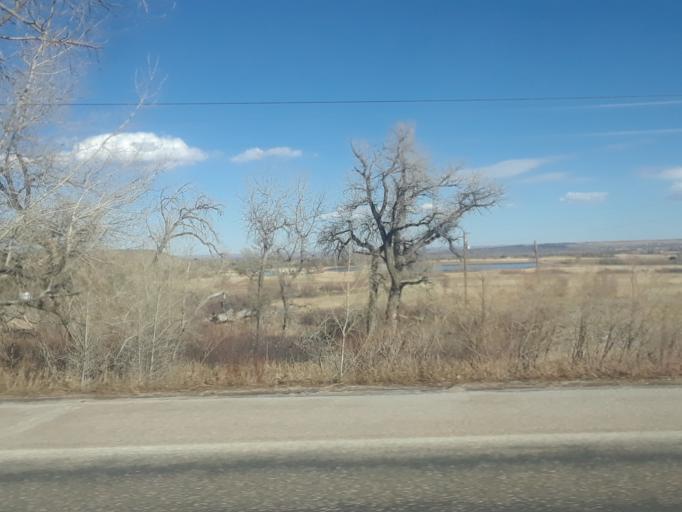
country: US
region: Colorado
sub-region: Boulder County
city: Boulder
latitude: 40.1110
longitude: -105.2820
